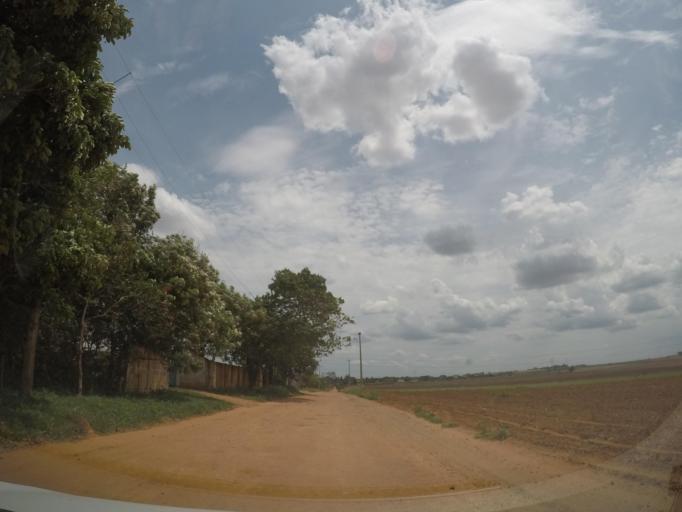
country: BR
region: Sao Paulo
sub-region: Sumare
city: Sumare
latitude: -22.8386
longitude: -47.2918
